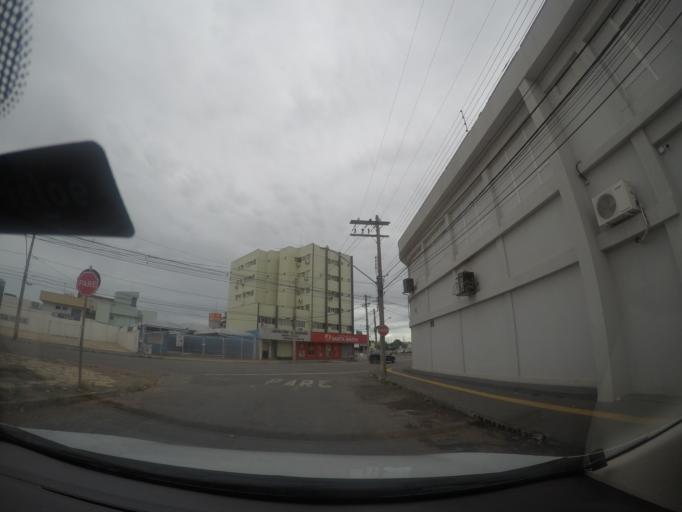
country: BR
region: Goias
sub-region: Goiania
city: Goiania
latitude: -16.6779
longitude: -49.2848
